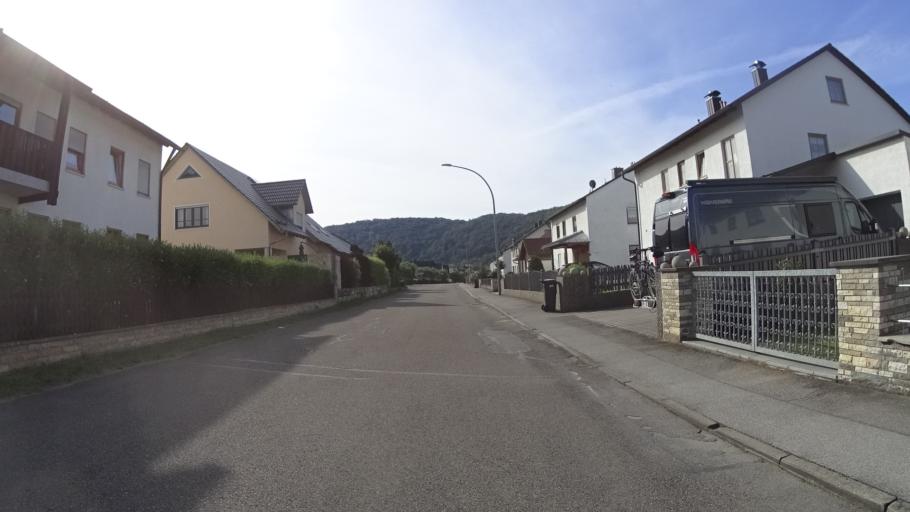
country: DE
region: Bavaria
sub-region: Lower Bavaria
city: Essing
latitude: 48.9283
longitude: 11.7972
